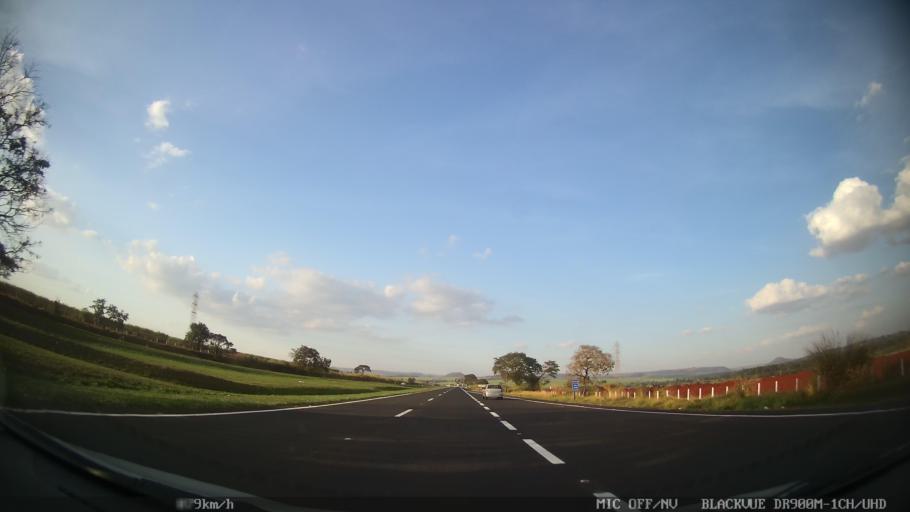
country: BR
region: Sao Paulo
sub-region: Ribeirao Preto
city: Ribeirao Preto
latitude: -21.1116
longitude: -47.7763
